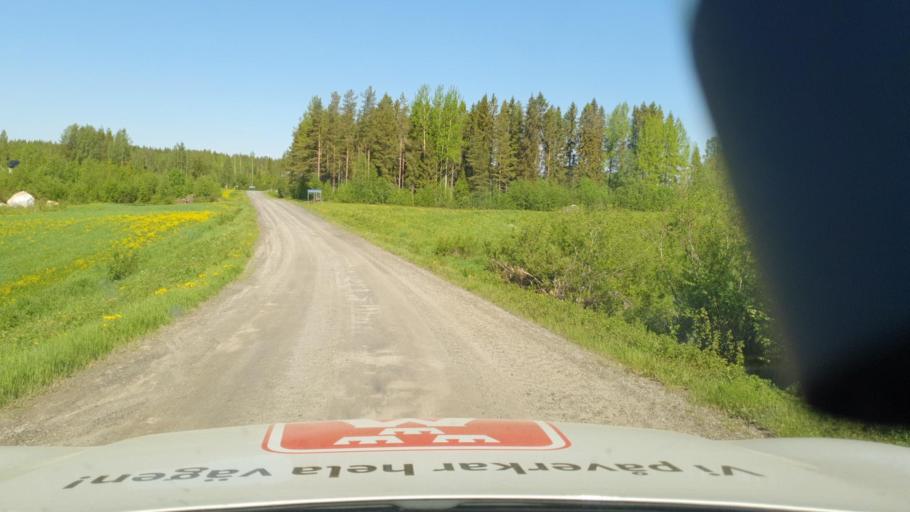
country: SE
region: Vaesterbotten
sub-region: Vannas Kommun
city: Vaennaes
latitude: 64.0202
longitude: 19.7599
